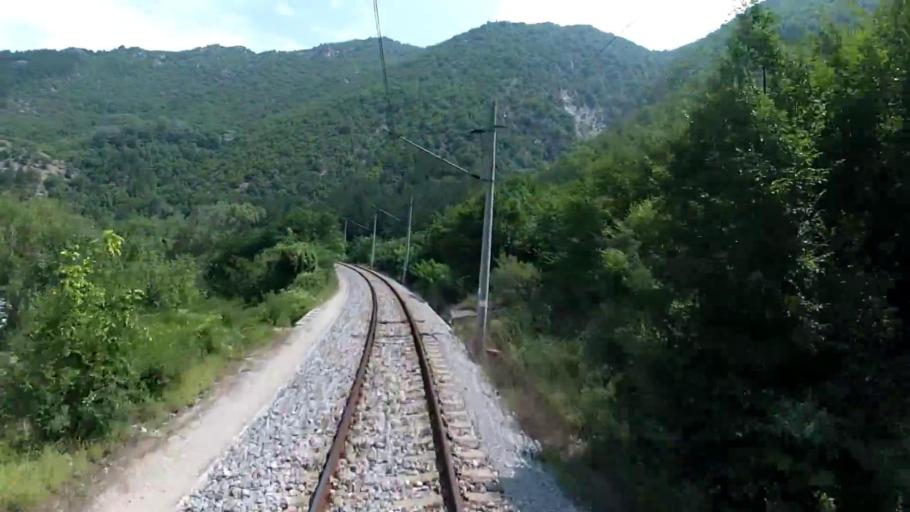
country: BG
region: Blagoevgrad
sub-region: Obshtina Kresna
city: Stara Kresna
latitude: 41.7775
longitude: 23.1555
